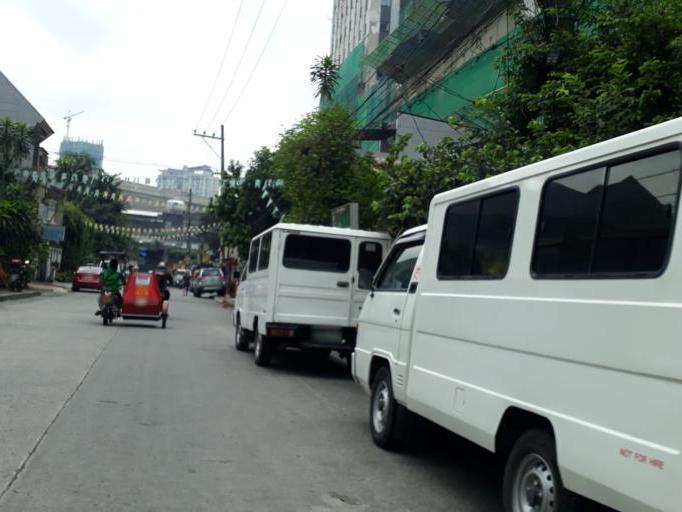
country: PH
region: Calabarzon
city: Bagong Pagasa
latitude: 14.6570
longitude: 121.0341
